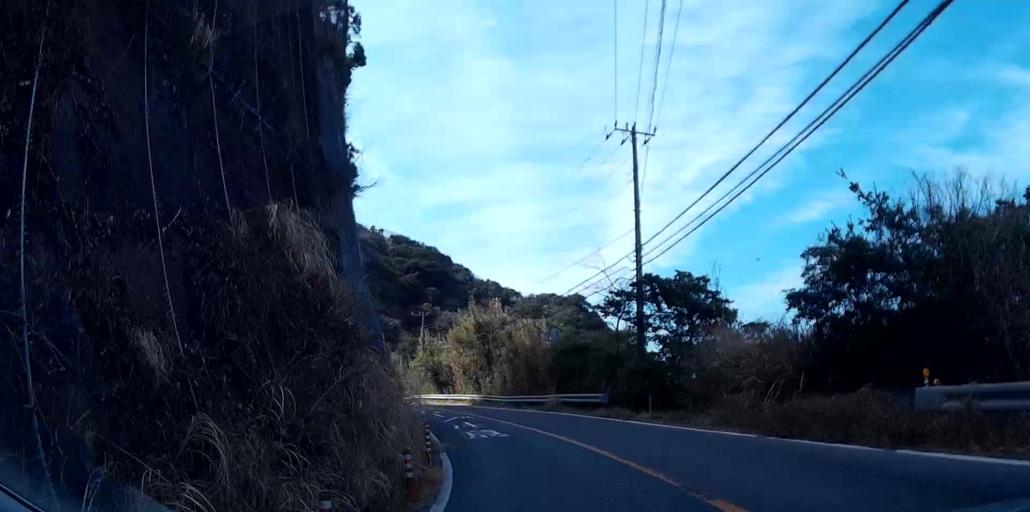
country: JP
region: Chiba
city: Tateyama
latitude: 34.9747
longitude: 139.7663
